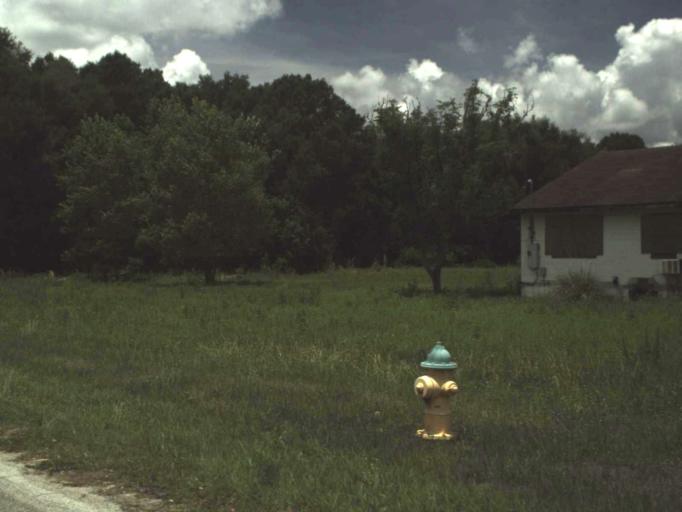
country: US
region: Florida
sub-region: Volusia County
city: DeLand
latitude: 29.0283
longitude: -81.2802
